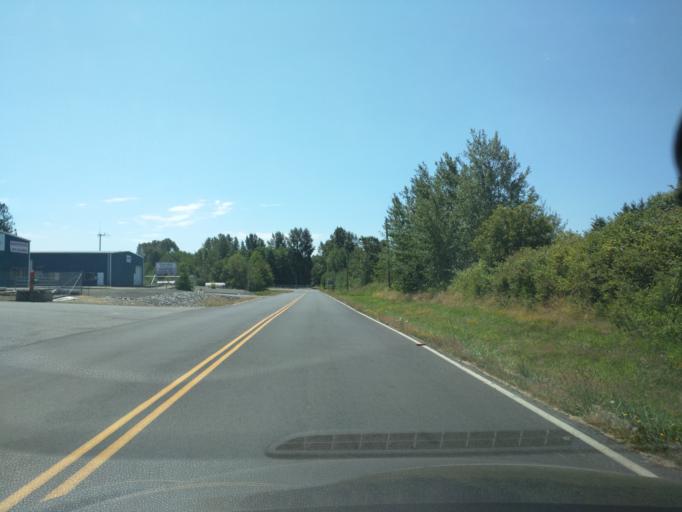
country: US
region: Washington
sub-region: Whatcom County
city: Blaine
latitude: 48.9893
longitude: -122.7345
